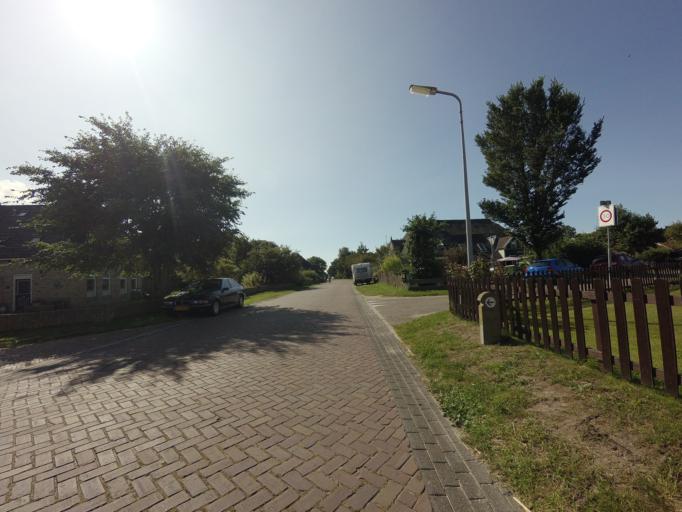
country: NL
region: Friesland
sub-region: Gemeente Terschelling
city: West-Terschelling
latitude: 53.4041
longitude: 5.3783
